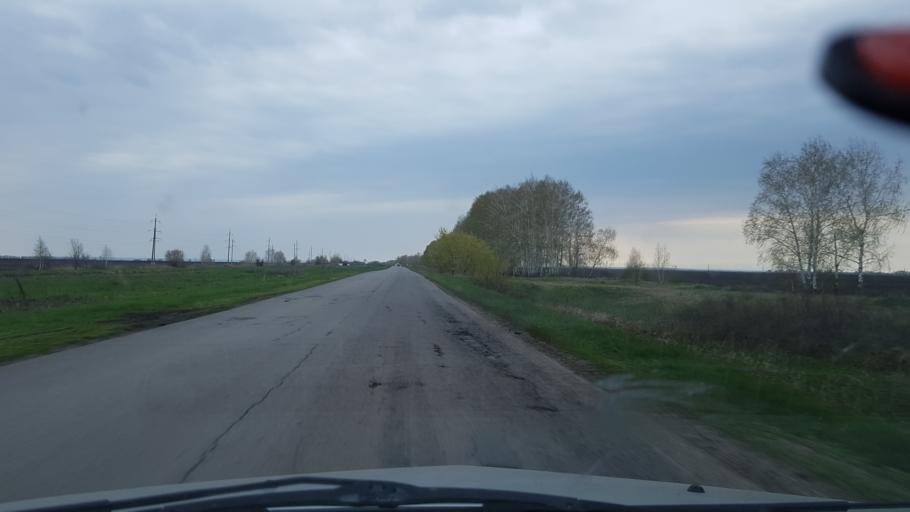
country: RU
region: Samara
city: Podstepki
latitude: 53.6662
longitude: 49.1624
